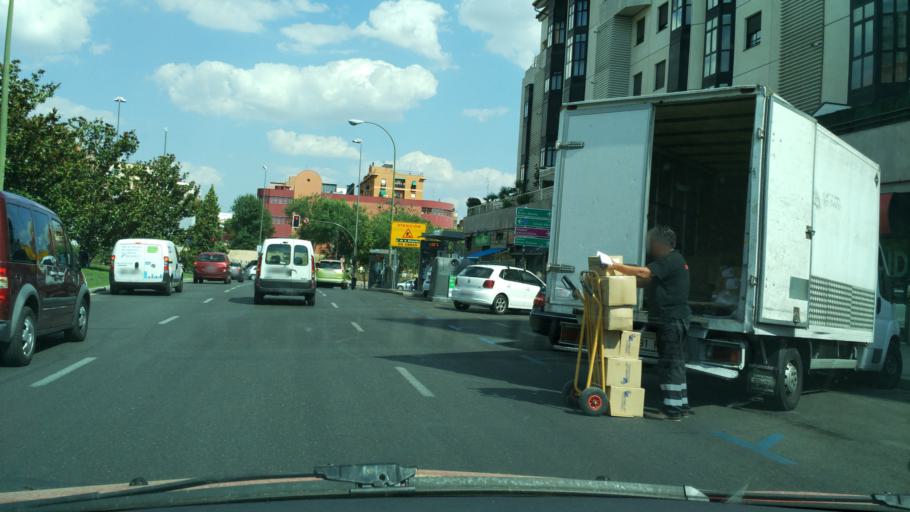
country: ES
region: Madrid
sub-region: Provincia de Madrid
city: Tetuan de las Victorias
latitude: 40.4577
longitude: -3.7127
